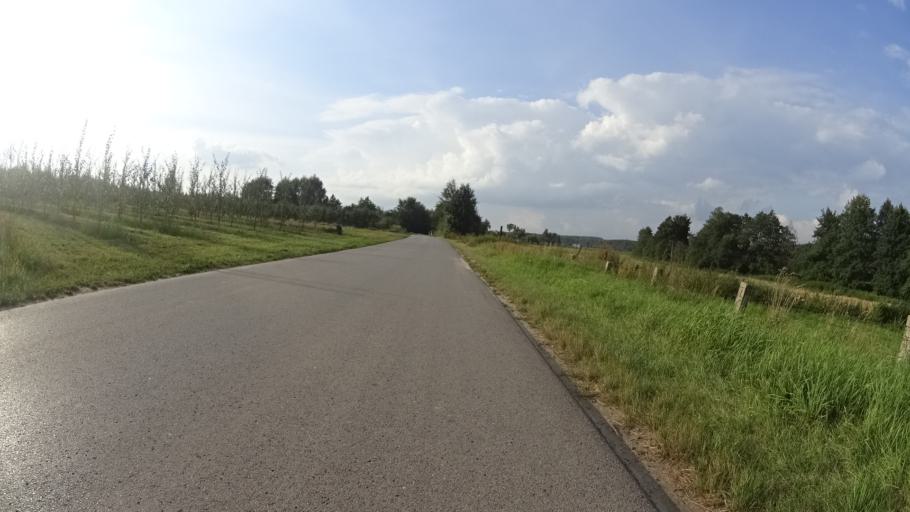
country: PL
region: Masovian Voivodeship
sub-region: Powiat grojecki
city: Mogielnica
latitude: 51.6804
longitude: 20.7331
